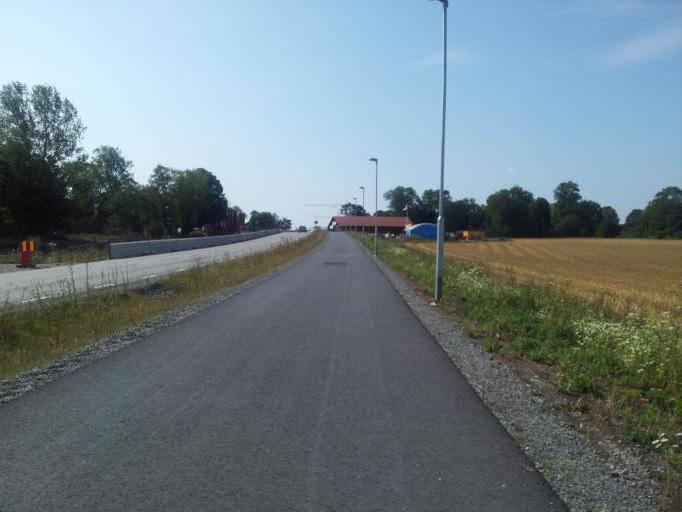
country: SE
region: Uppsala
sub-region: Uppsala Kommun
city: Gamla Uppsala
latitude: 59.9008
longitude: 17.6392
